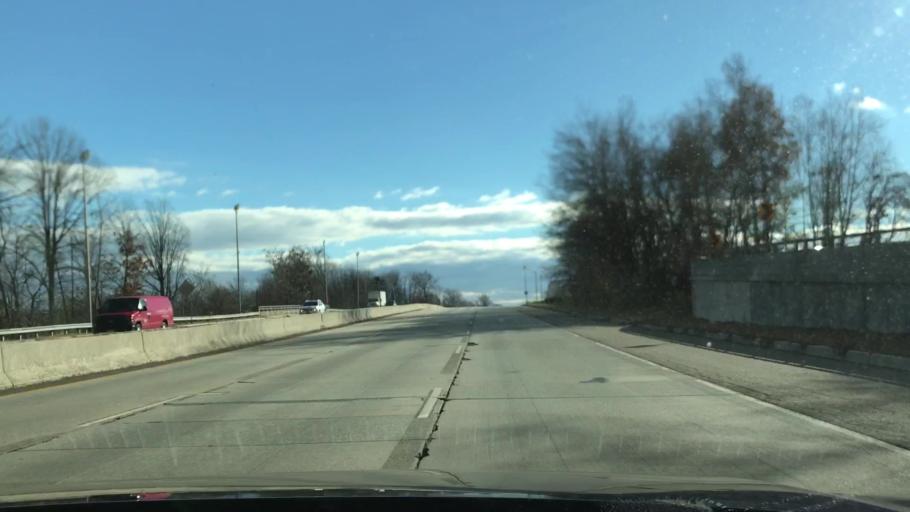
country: US
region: New Jersey
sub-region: Passaic County
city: Passaic
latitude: 40.8520
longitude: -74.1220
